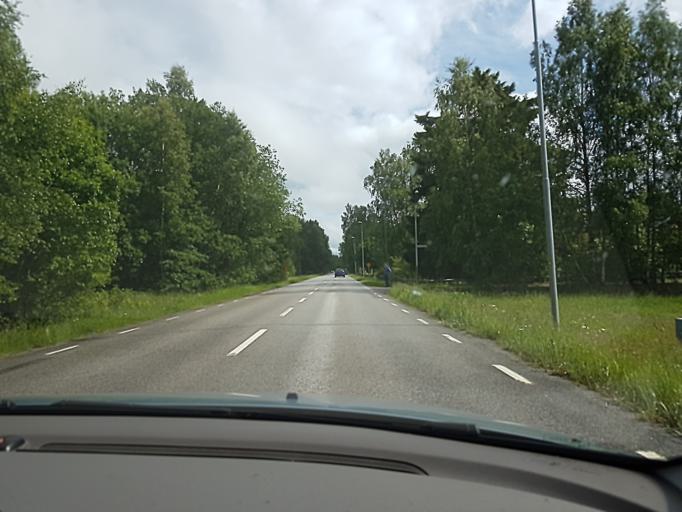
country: SE
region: Uppsala
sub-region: Osthammars Kommun
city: OEsthammar
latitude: 60.2796
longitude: 18.2987
